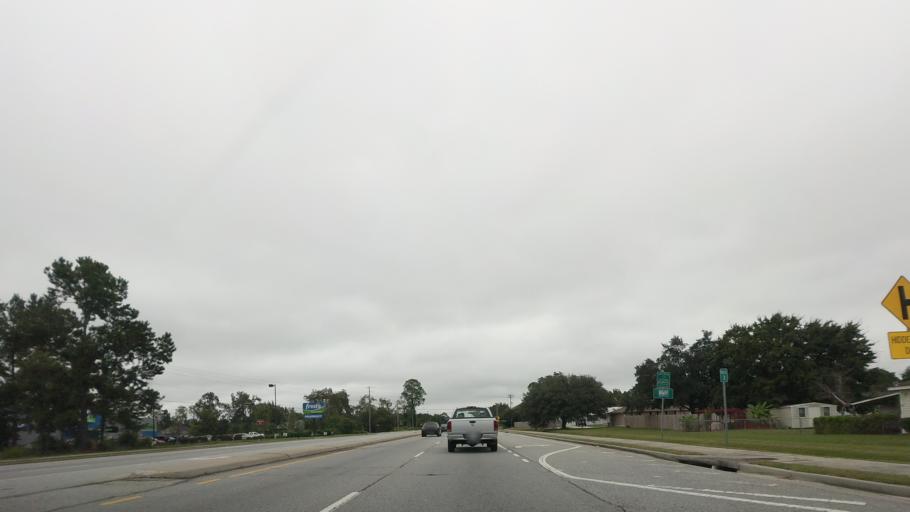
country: US
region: Georgia
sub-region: Lowndes County
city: Valdosta
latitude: 30.9216
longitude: -83.2521
